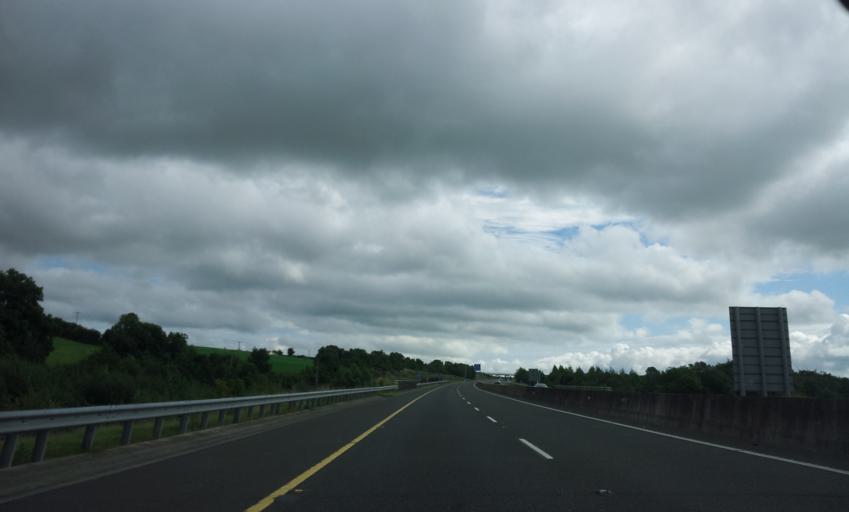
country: IE
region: Munster
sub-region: North Tipperary
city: Nenagh
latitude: 52.8565
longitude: -8.1343
